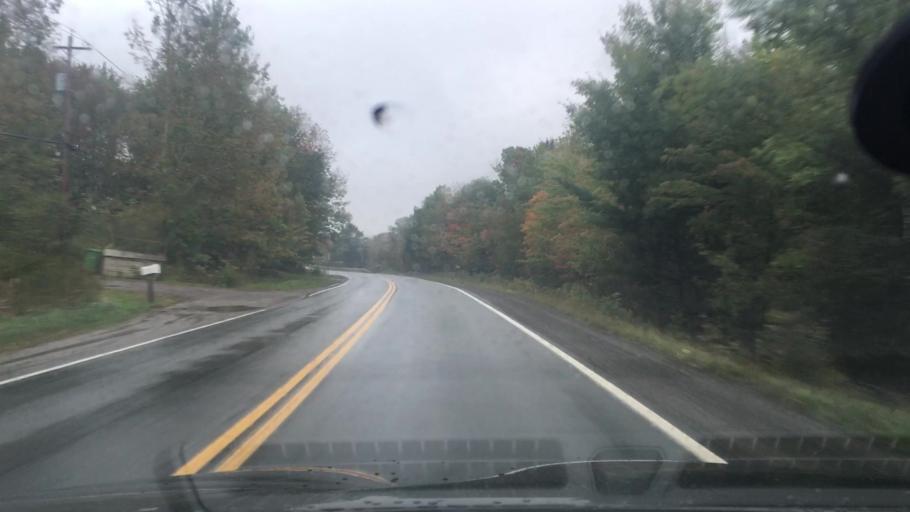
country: CA
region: Nova Scotia
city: Windsor
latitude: 44.8432
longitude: -64.2287
